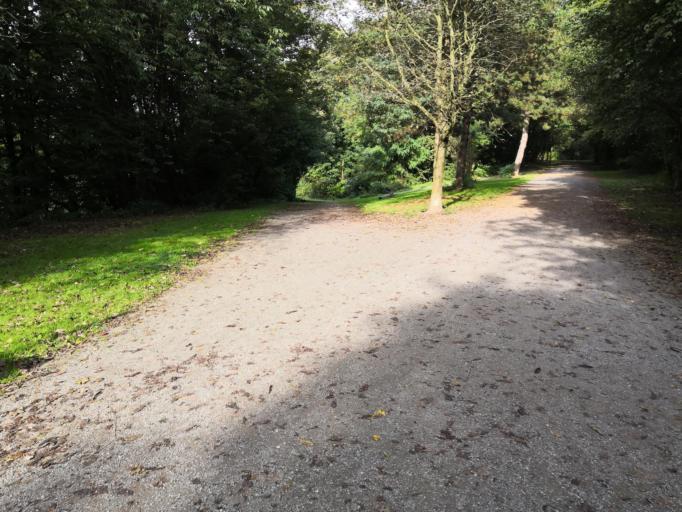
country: DE
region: North Rhine-Westphalia
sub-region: Regierungsbezirk Dusseldorf
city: Moers
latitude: 51.4060
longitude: 6.6837
